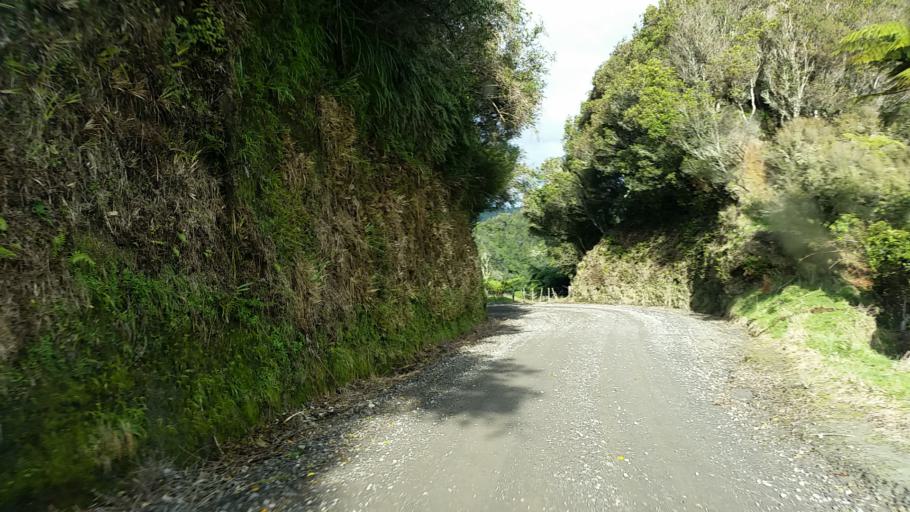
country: NZ
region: Taranaki
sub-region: South Taranaki District
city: Eltham
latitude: -39.1756
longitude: 174.6278
